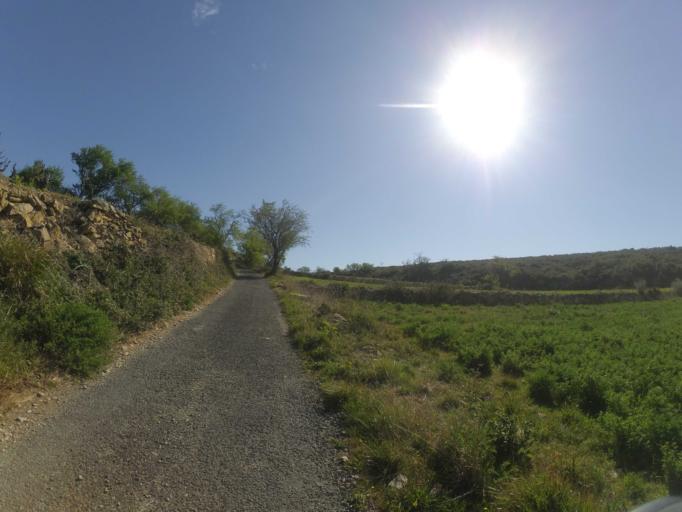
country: FR
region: Languedoc-Roussillon
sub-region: Departement des Pyrenees-Orientales
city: Baixas
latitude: 42.7617
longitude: 2.7562
